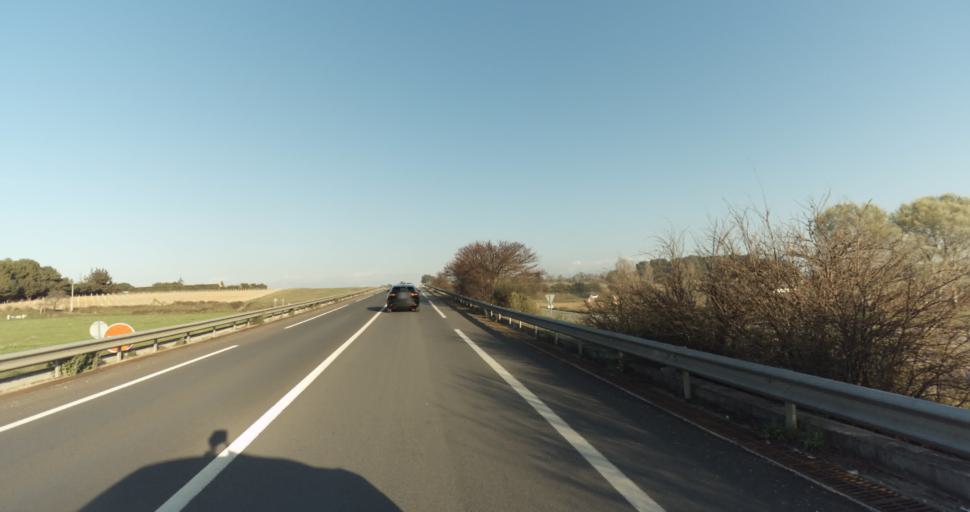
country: FR
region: Provence-Alpes-Cote d'Azur
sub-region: Departement des Bouches-du-Rhone
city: Eguilles
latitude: 43.5446
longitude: 5.3464
